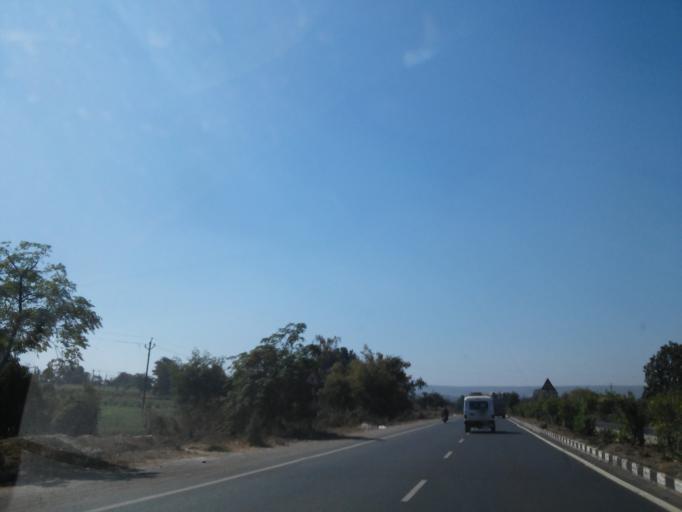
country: IN
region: Gujarat
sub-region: Sabar Kantha
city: Meghraj
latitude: 23.7370
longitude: 73.4202
